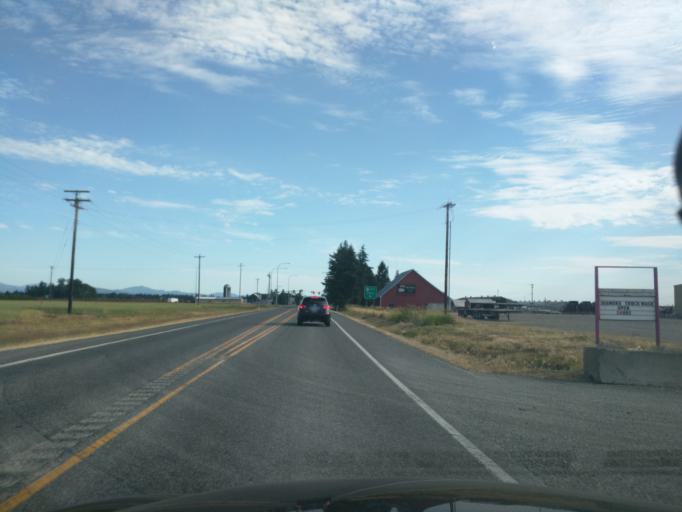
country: US
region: Washington
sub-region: Whatcom County
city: Lynden
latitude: 48.9665
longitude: -122.4853
